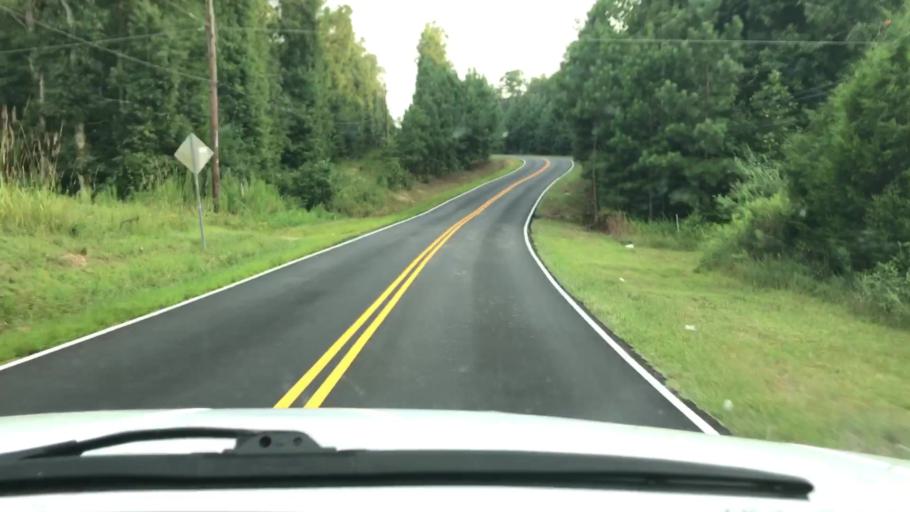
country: US
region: Virginia
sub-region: Chesterfield County
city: Chesterfield
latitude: 37.4214
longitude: -77.5352
